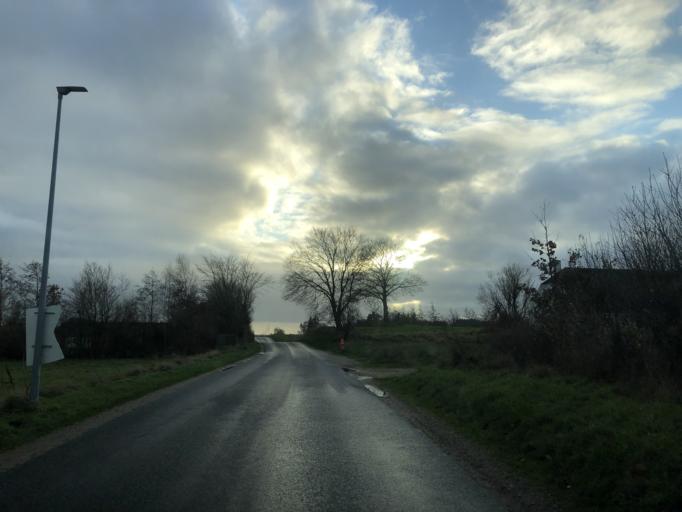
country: DK
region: Central Jutland
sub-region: Viborg Kommune
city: Viborg
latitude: 56.4800
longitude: 9.3430
